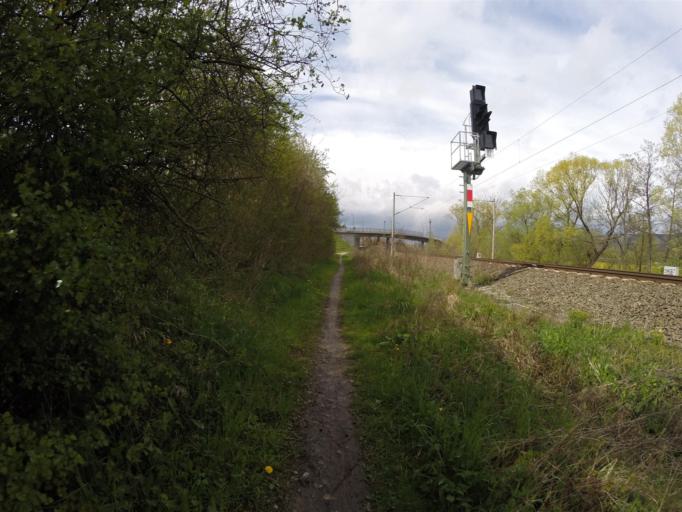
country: DE
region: Thuringia
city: Sulza
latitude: 50.8762
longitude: 11.5949
